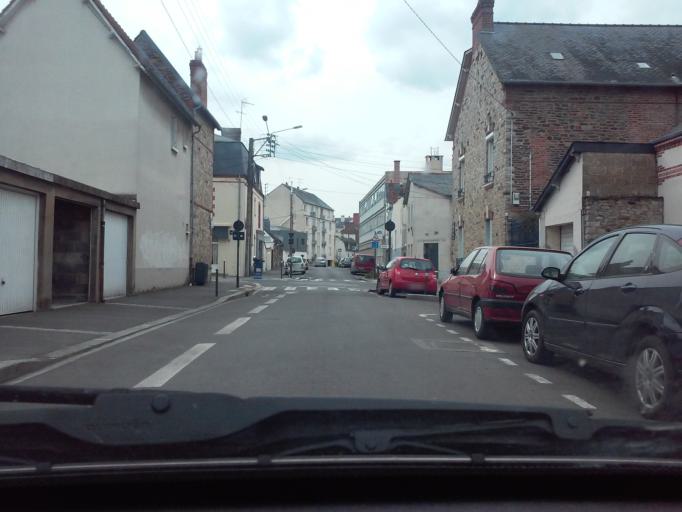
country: FR
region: Brittany
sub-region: Departement d'Ille-et-Vilaine
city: Rennes
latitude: 48.0990
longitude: -1.6837
